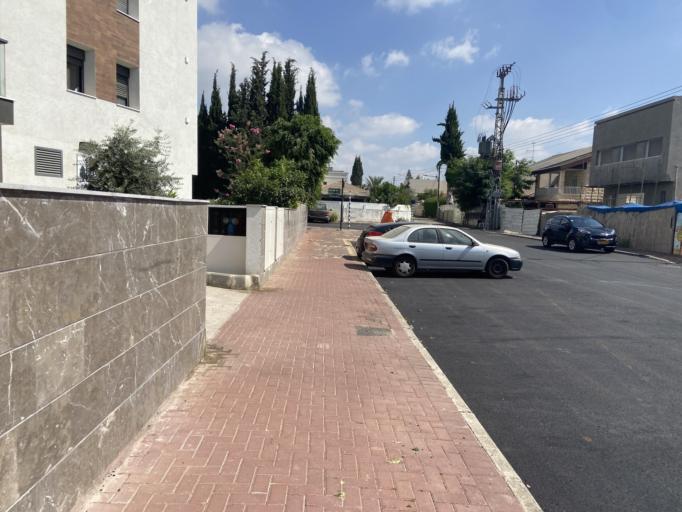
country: IL
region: Central District
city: Yehud
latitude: 32.0364
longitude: 34.8907
